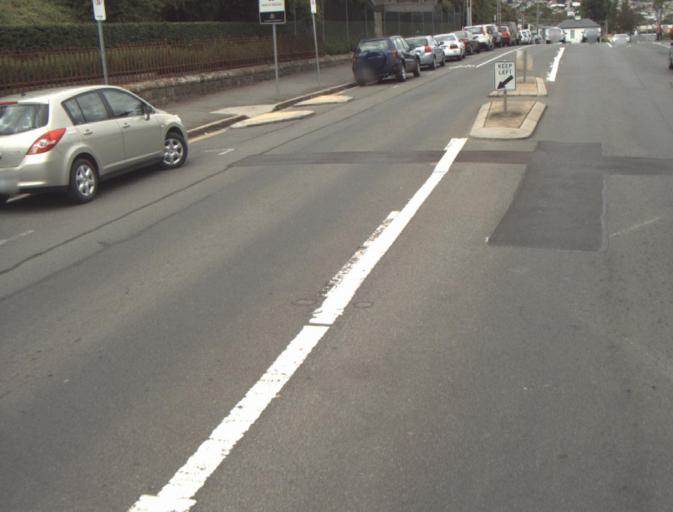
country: AU
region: Tasmania
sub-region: Launceston
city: Launceston
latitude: -41.4462
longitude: 147.1428
